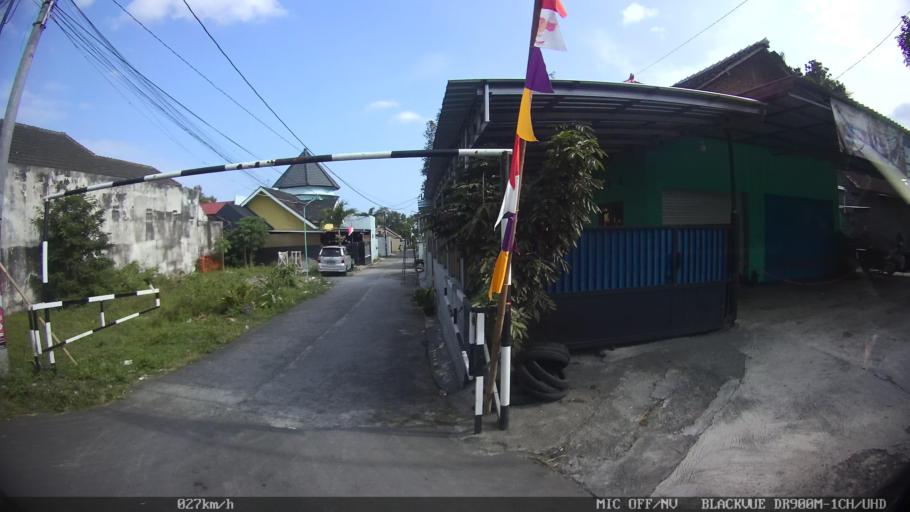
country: ID
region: Daerah Istimewa Yogyakarta
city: Depok
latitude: -7.7355
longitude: 110.4357
